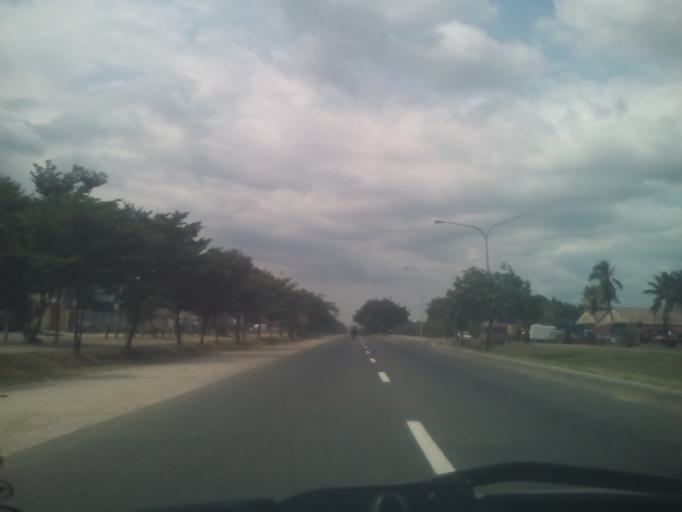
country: TZ
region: Dar es Salaam
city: Dar es Salaam
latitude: -6.8374
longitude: 39.2589
